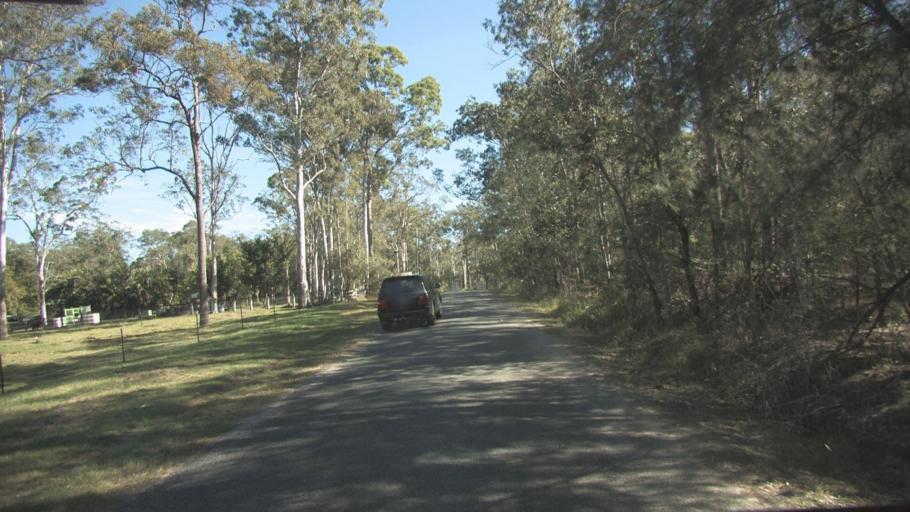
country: AU
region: Queensland
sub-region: Ipswich
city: Springfield Lakes
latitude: -27.7146
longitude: 152.9392
